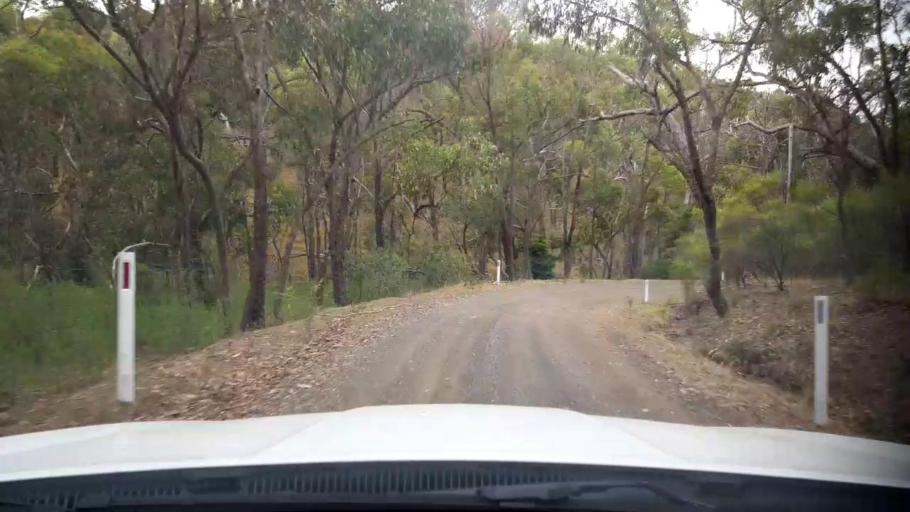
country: AU
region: Victoria
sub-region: Whittlesea
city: Whittlesea
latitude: -37.4832
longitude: 145.0506
